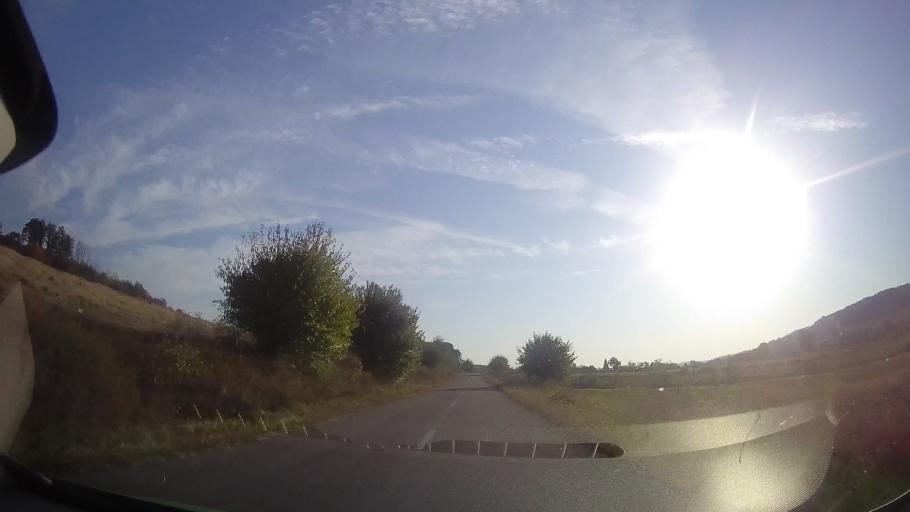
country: RO
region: Timis
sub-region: Comuna Bogda
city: Bogda
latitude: 45.9822
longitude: 21.5467
